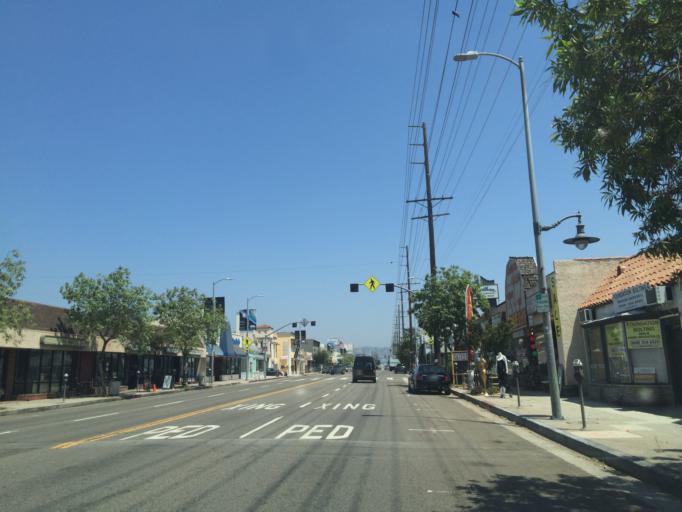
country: US
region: California
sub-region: Los Angeles County
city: Culver City
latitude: 34.0358
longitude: -118.3890
